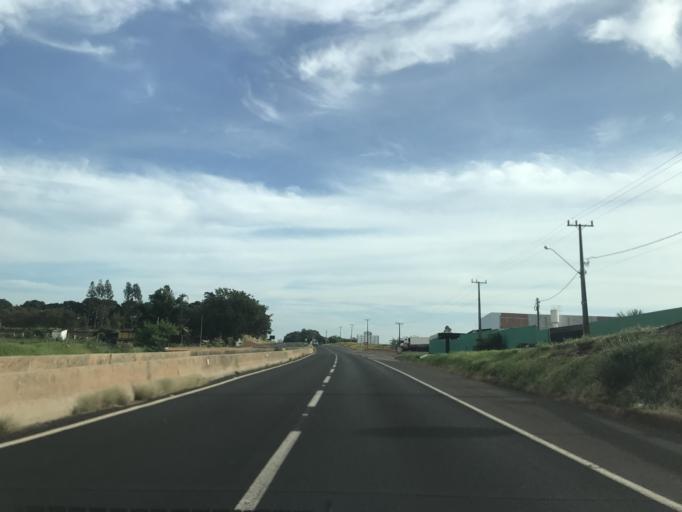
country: BR
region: Parana
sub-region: Mandaguacu
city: Mandaguacu
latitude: -23.3185
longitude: -52.1097
